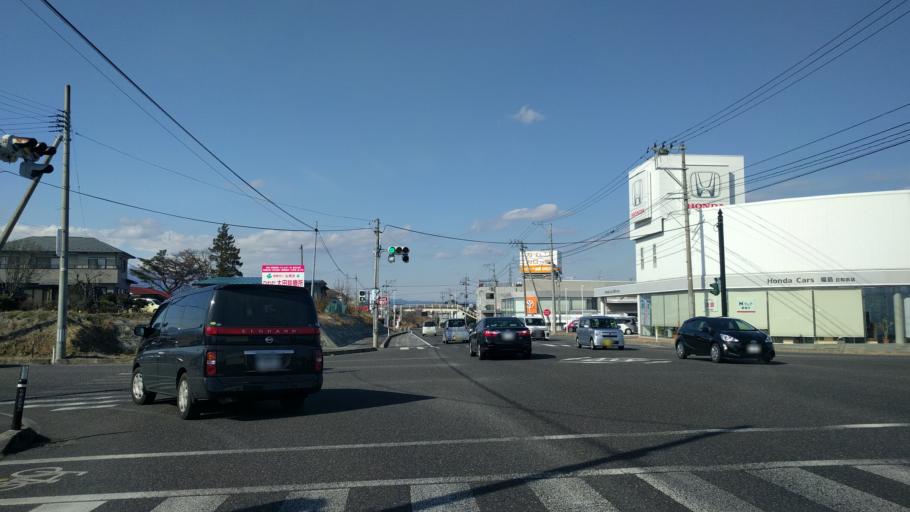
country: JP
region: Fukushima
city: Koriyama
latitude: 37.4411
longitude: 140.3797
